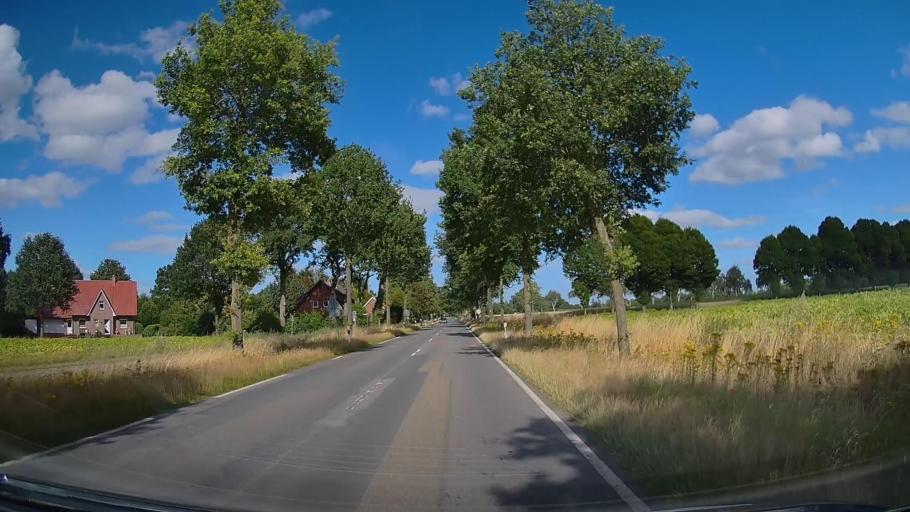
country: DE
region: Lower Saxony
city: Berge
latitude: 52.6239
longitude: 7.7675
